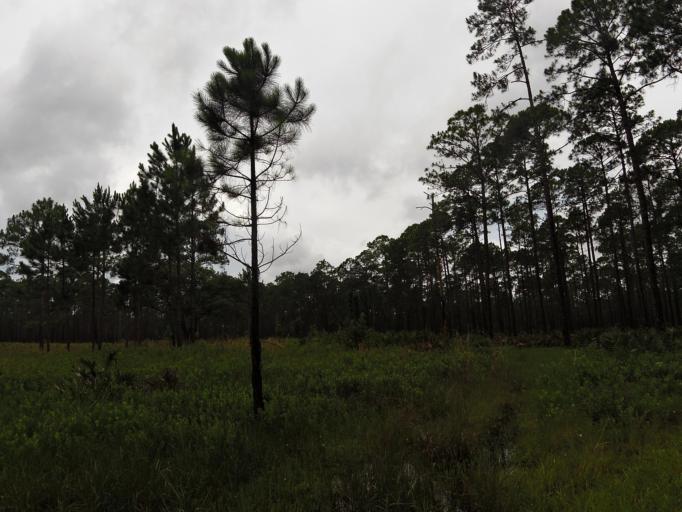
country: US
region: Florida
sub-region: Clay County
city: Green Cove Springs
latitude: 29.9691
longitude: -81.6300
